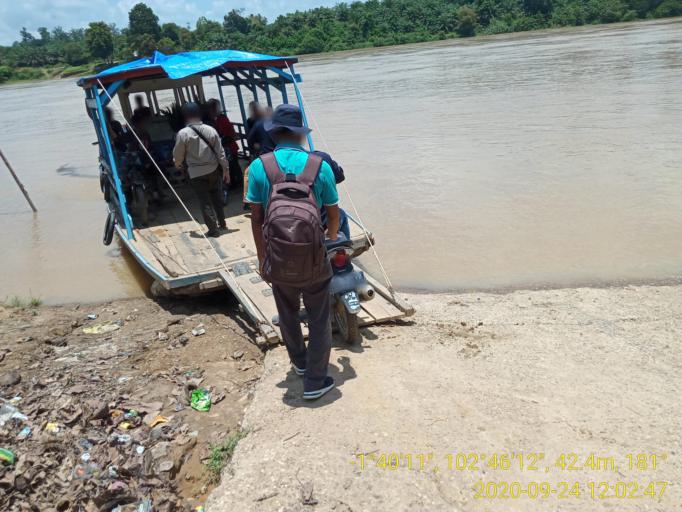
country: ID
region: Jambi
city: Sungaibengkal
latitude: -1.6700
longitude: 102.7703
